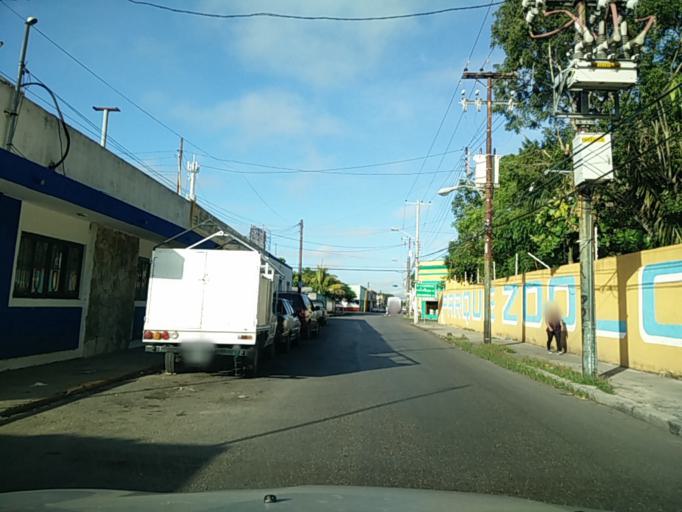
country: MX
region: Yucatan
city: Merida
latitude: 20.9665
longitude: -89.6402
